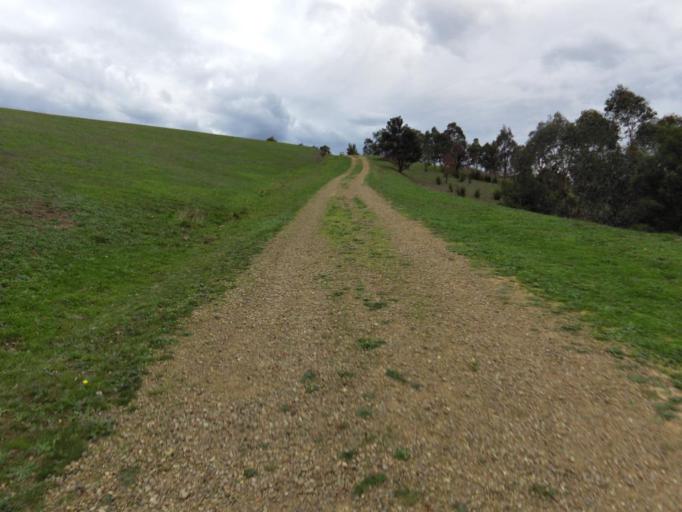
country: AU
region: Victoria
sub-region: Yarra Ranges
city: Chirnside Park
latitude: -37.7135
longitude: 145.2901
